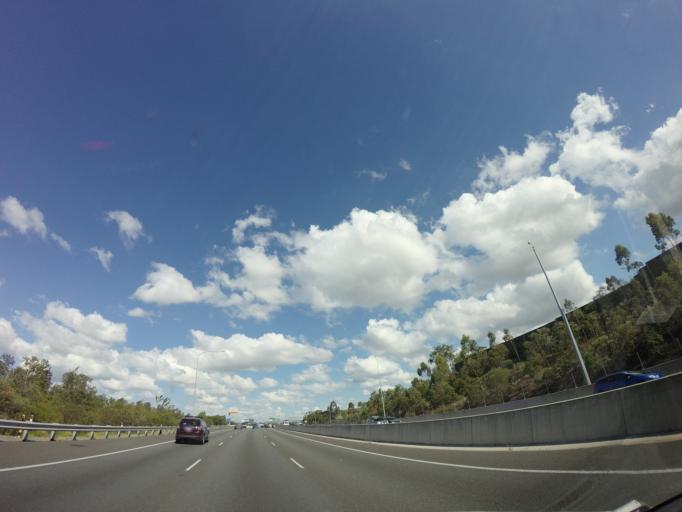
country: AU
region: Queensland
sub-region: Ipswich
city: Redbank
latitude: -27.6015
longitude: 152.8846
